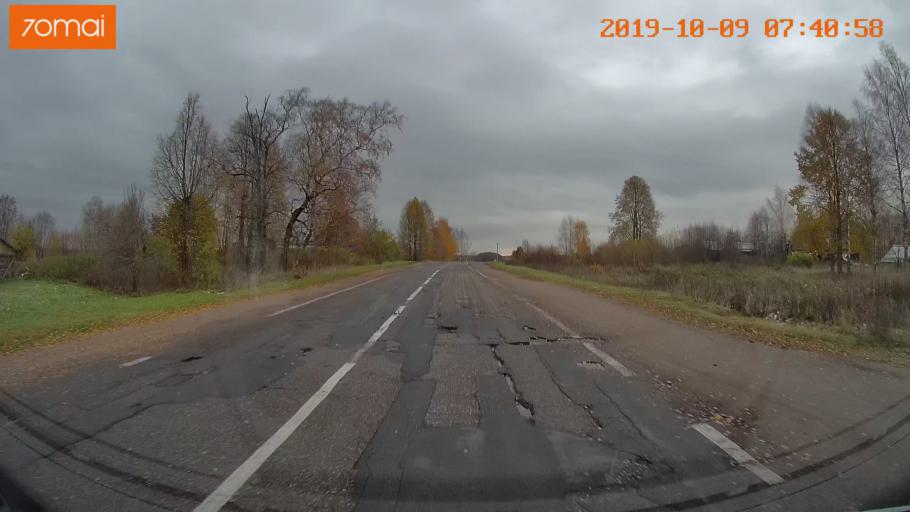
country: RU
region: Jaroslavl
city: Kukoboy
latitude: 58.6368
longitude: 39.7004
